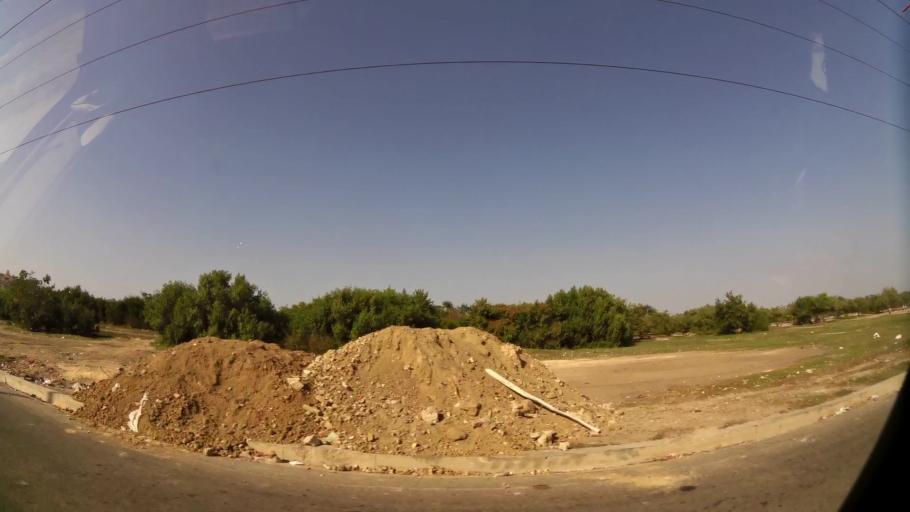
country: CO
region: Bolivar
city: Cartagena
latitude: 10.4156
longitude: -75.5105
